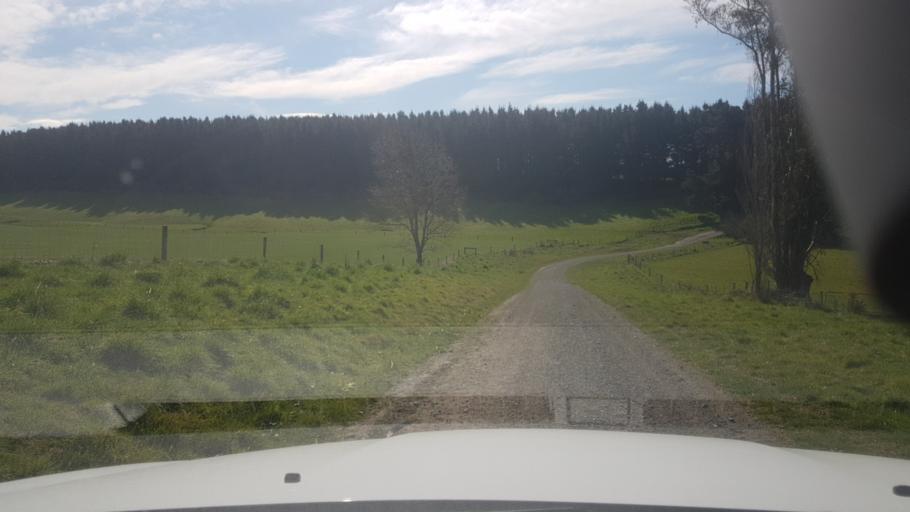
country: NZ
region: Canterbury
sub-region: Timaru District
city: Pleasant Point
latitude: -44.1976
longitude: 171.1875
